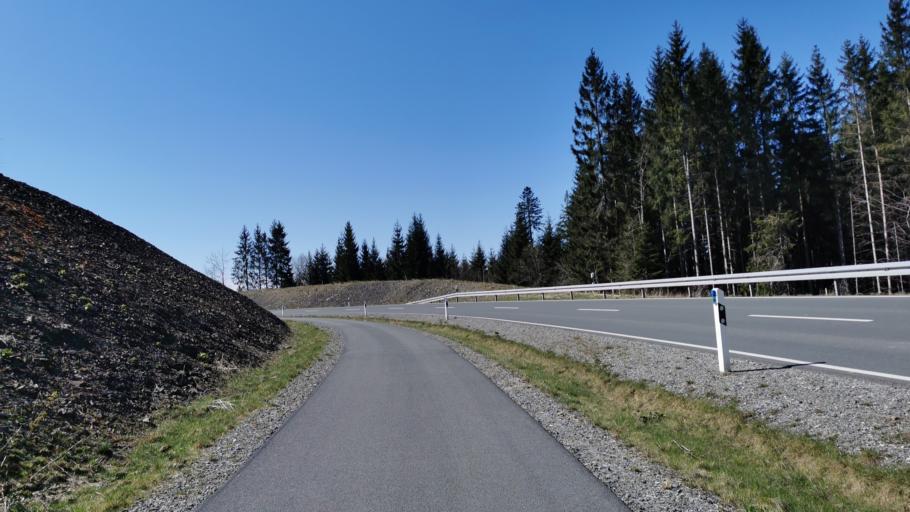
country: DE
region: Bavaria
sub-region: Upper Franconia
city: Teuschnitz
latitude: 50.4197
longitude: 11.3334
